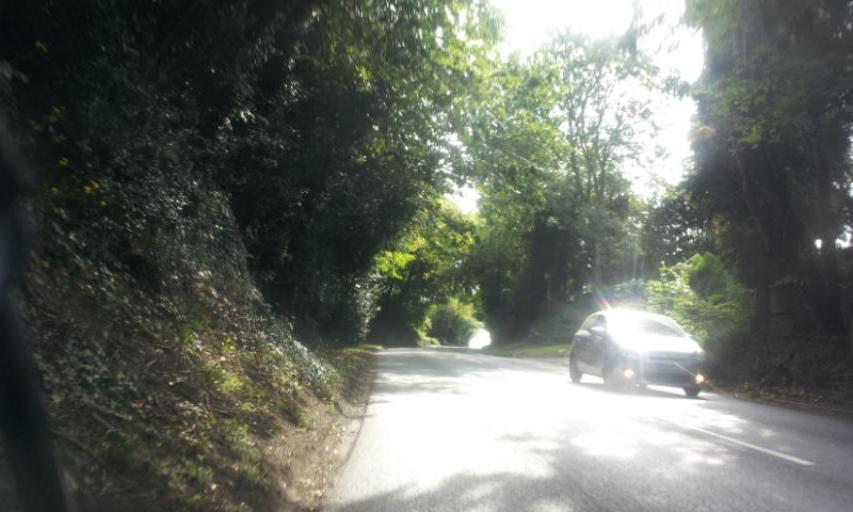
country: GB
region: England
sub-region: Kent
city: Paddock Wood
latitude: 51.1597
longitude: 0.3790
